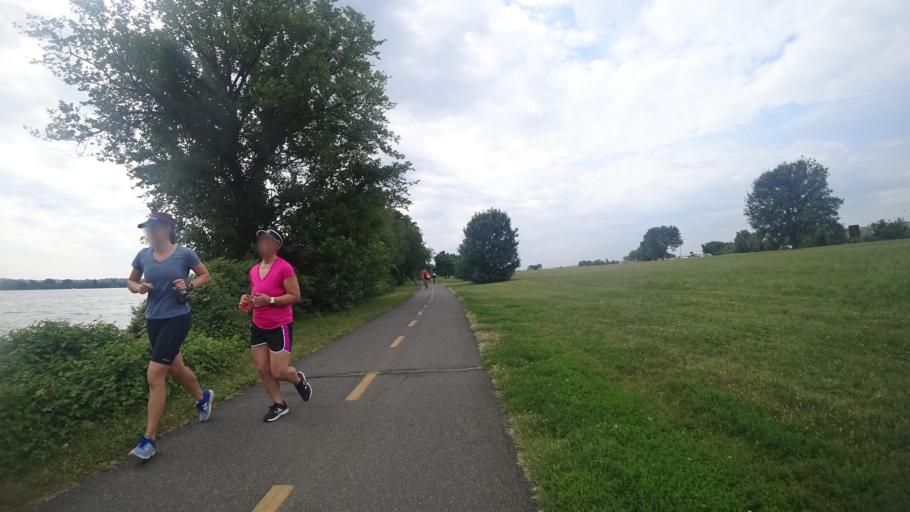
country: US
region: Washington, D.C.
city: Washington, D.C.
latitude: 38.8693
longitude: -77.0393
